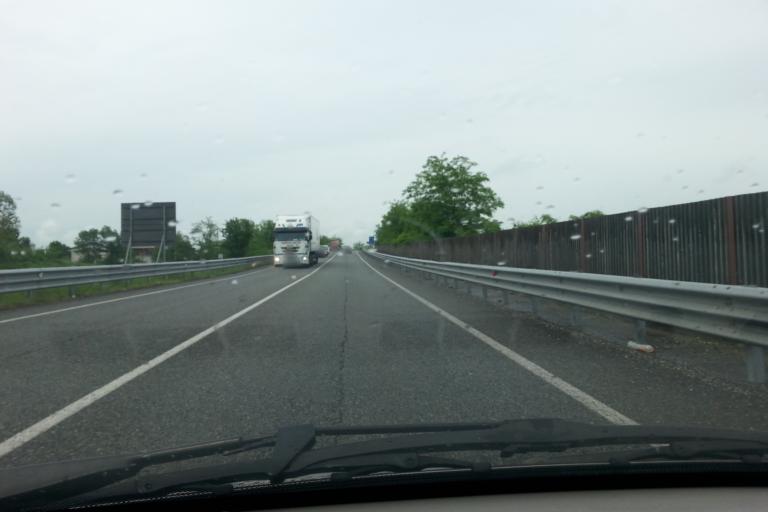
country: IT
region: Piedmont
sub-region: Provincia di Torino
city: Alpignano
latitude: 45.1177
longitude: 7.5155
